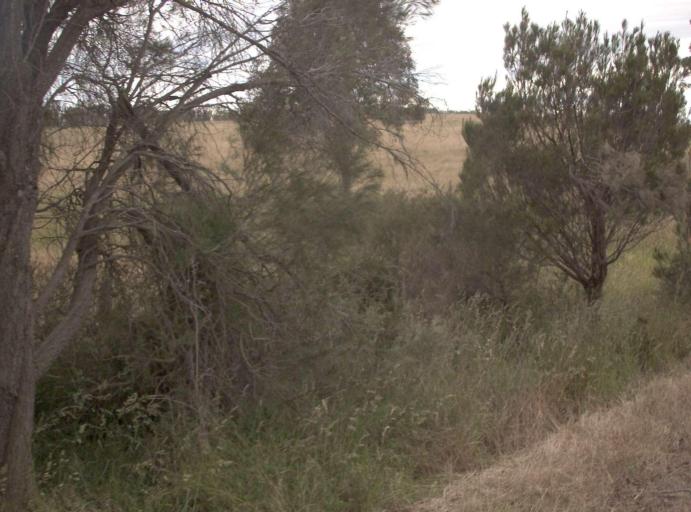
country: AU
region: Victoria
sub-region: East Gippsland
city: Bairnsdale
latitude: -37.9772
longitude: 147.4232
